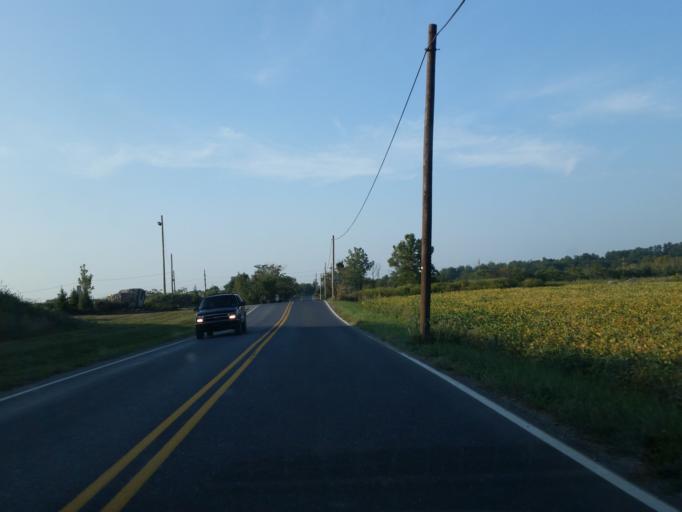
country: US
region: Pennsylvania
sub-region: Lebanon County
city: Annville
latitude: 40.3267
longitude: -76.5409
